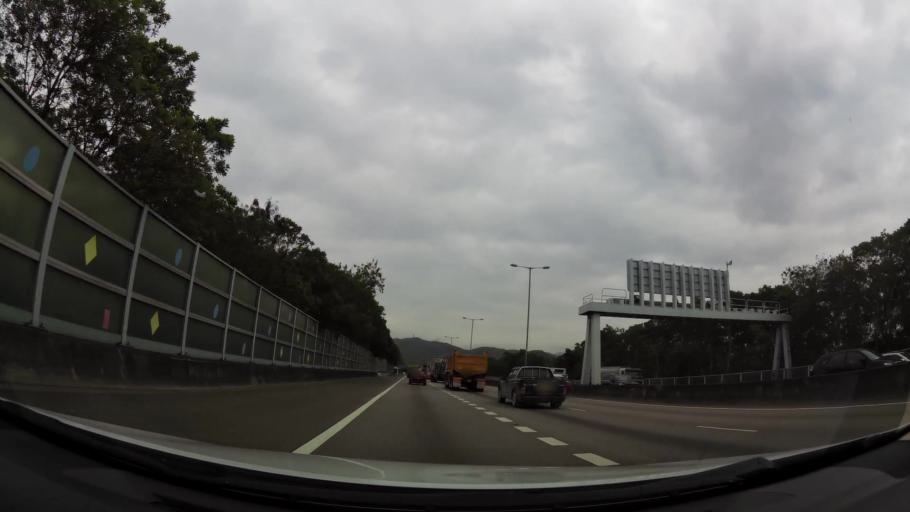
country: HK
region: Yuen Long
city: Yuen Long Kau Hui
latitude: 22.4346
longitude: 114.0267
